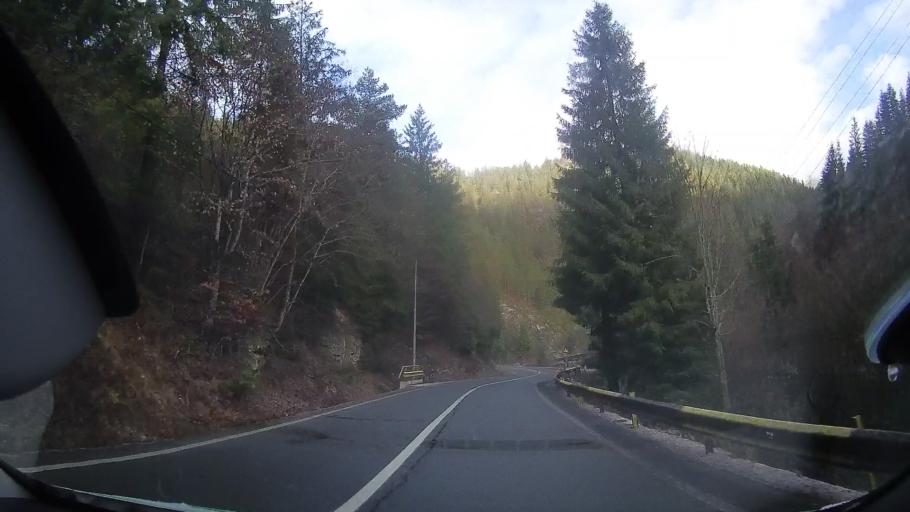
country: RO
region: Alba
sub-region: Comuna Albac
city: Albac
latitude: 46.4550
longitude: 22.9324
